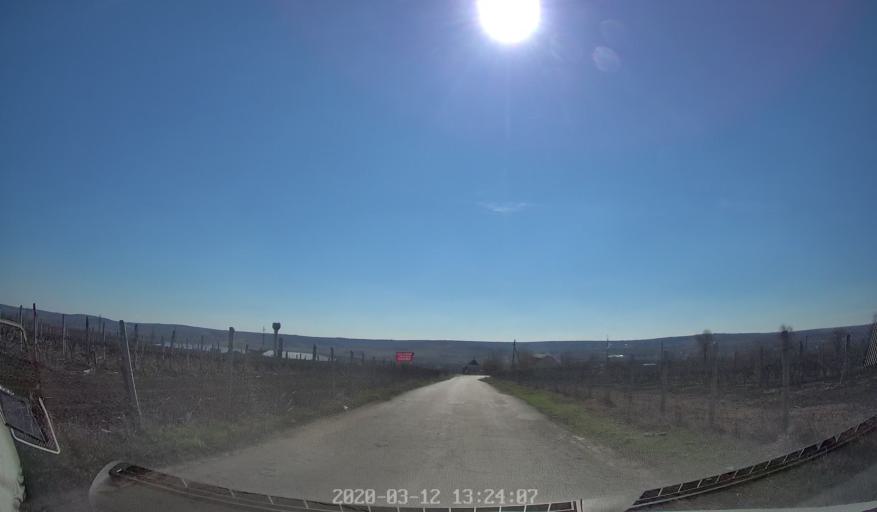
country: MD
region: Laloveni
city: Ialoveni
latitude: 46.9407
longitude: 28.8313
